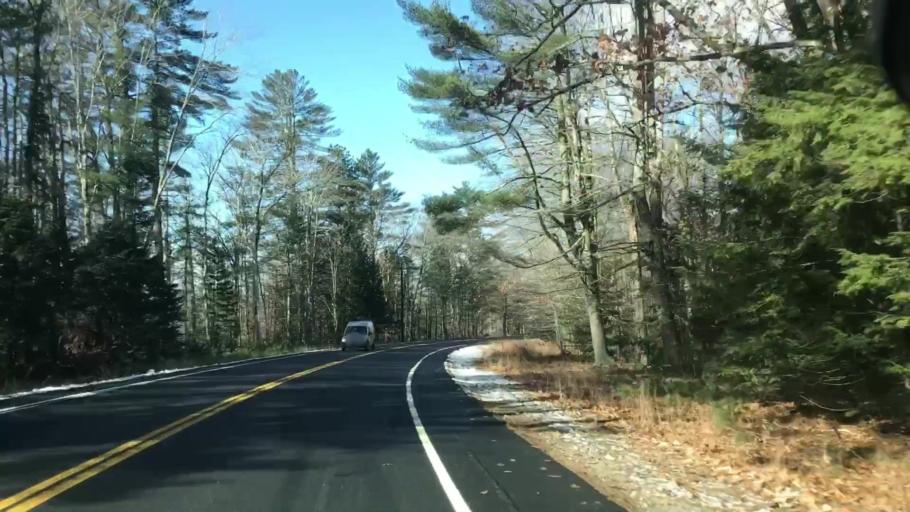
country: US
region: New Hampshire
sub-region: Carroll County
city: Effingham
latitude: 43.7889
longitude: -70.9752
